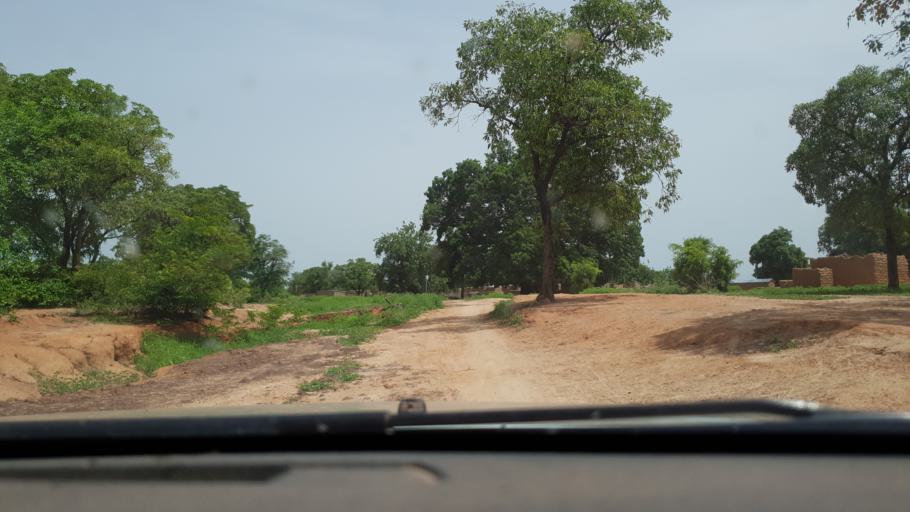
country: ML
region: Koulikoro
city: Koulikoro
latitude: 12.6694
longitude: -7.2455
